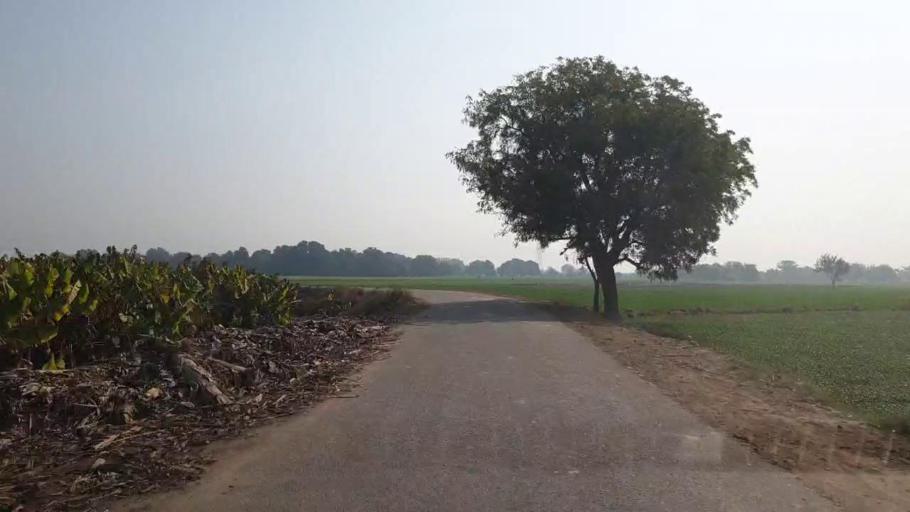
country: PK
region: Sindh
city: Bhit Shah
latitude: 25.7360
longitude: 68.5114
